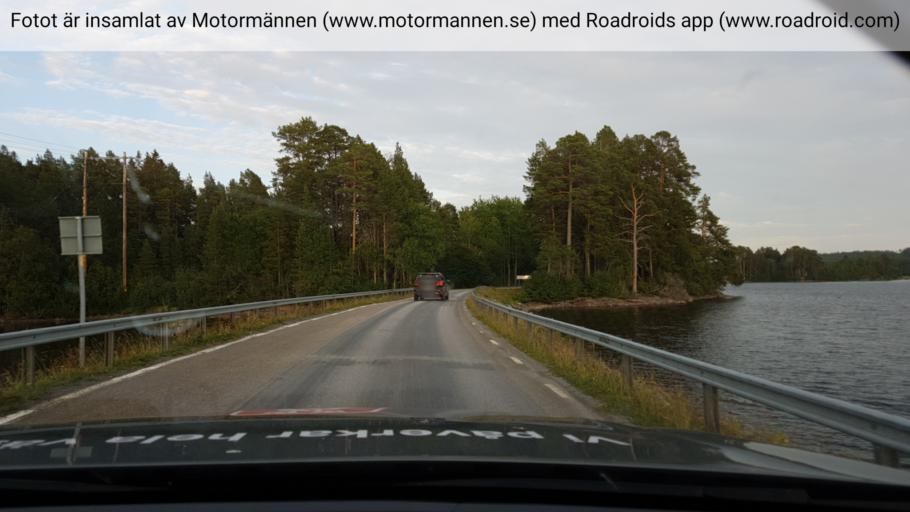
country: SE
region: Jaemtland
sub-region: Krokoms Kommun
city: Krokom
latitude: 63.1323
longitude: 14.4213
